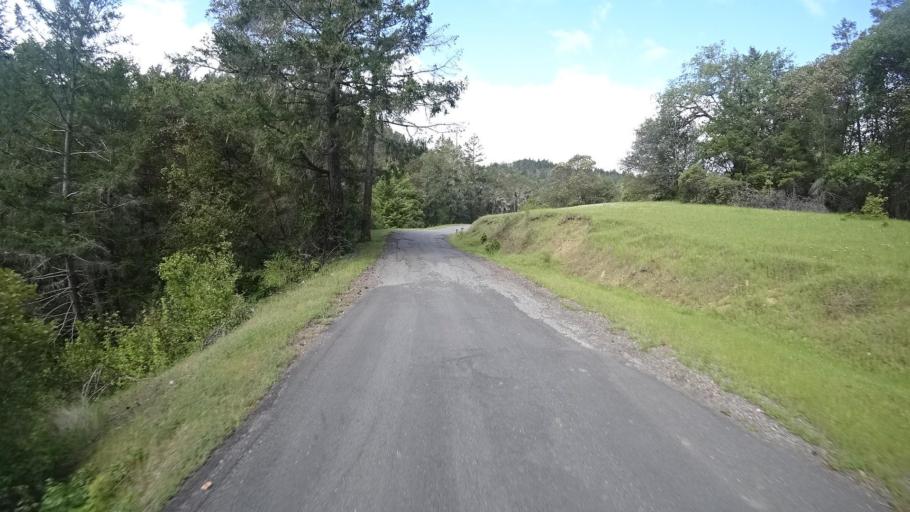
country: US
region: California
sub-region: Humboldt County
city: Redway
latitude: 40.2156
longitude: -123.6513
